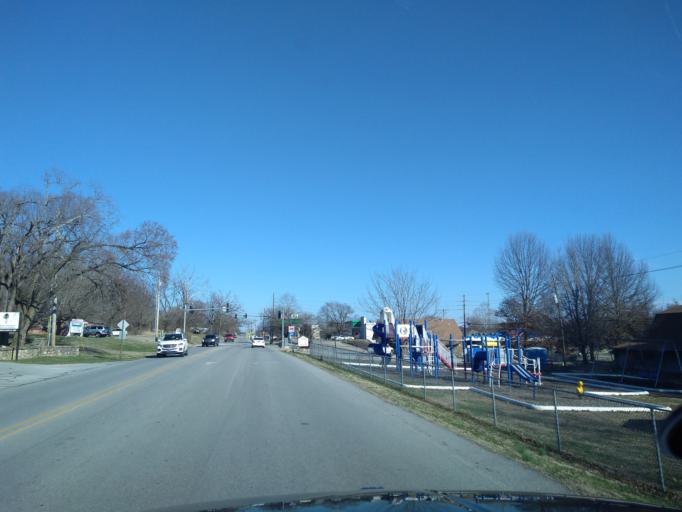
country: US
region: Arkansas
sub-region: Washington County
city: Johnson
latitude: 36.1335
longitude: -94.1642
